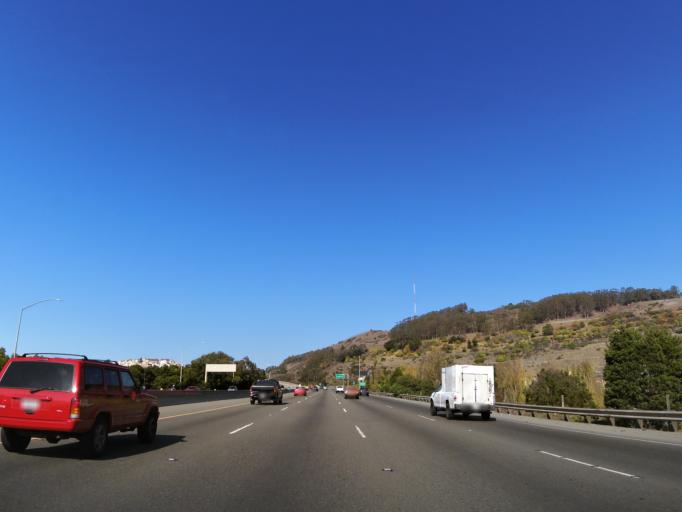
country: US
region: California
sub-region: San Mateo County
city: Brisbane
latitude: 37.7089
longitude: -122.3950
